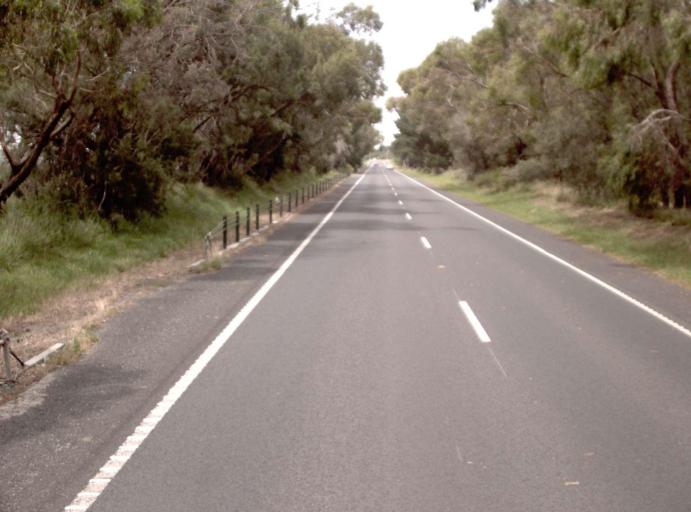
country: AU
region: Victoria
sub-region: Mornington Peninsula
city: Tyabb
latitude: -38.2461
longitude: 145.2150
